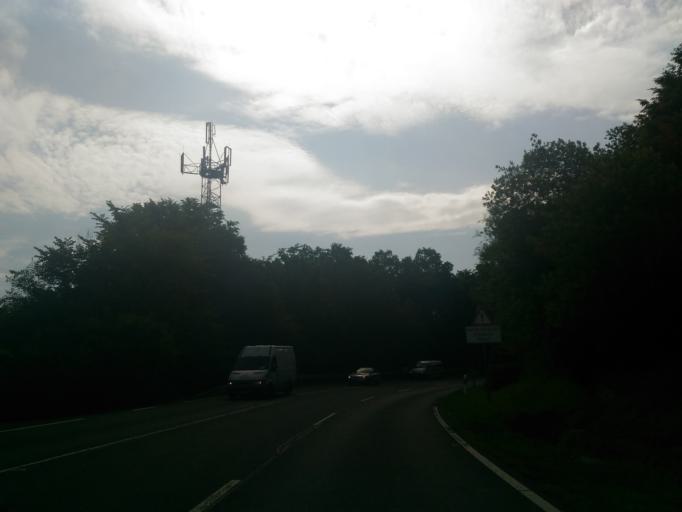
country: HU
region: Baranya
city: Komlo
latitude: 46.1569
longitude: 18.2420
